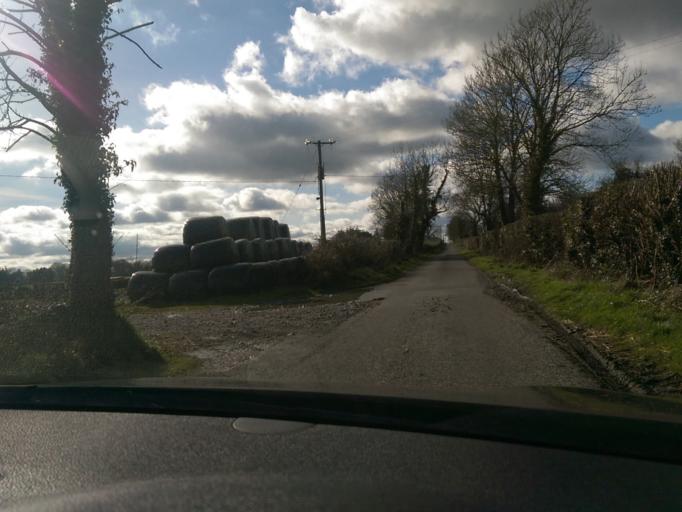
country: IE
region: Connaught
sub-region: County Galway
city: Athenry
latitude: 53.4667
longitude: -8.5662
